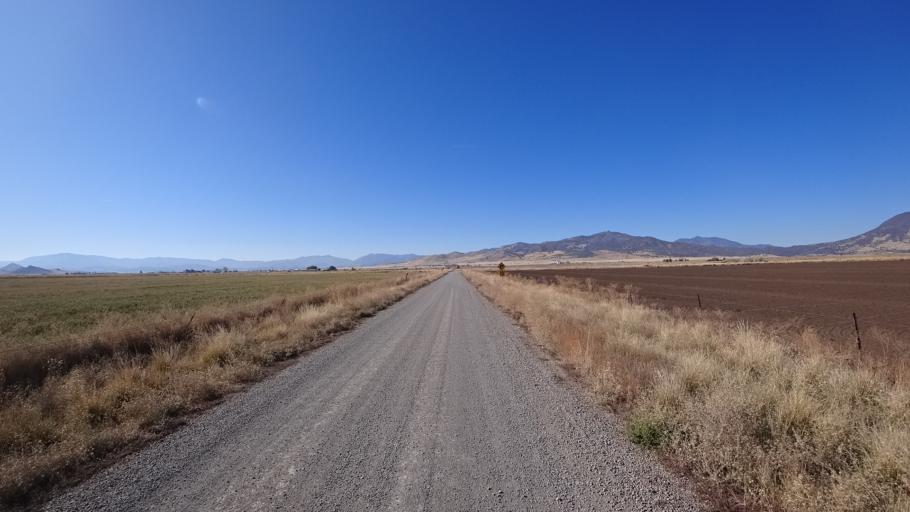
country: US
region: California
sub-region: Siskiyou County
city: Montague
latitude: 41.7864
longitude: -122.4587
